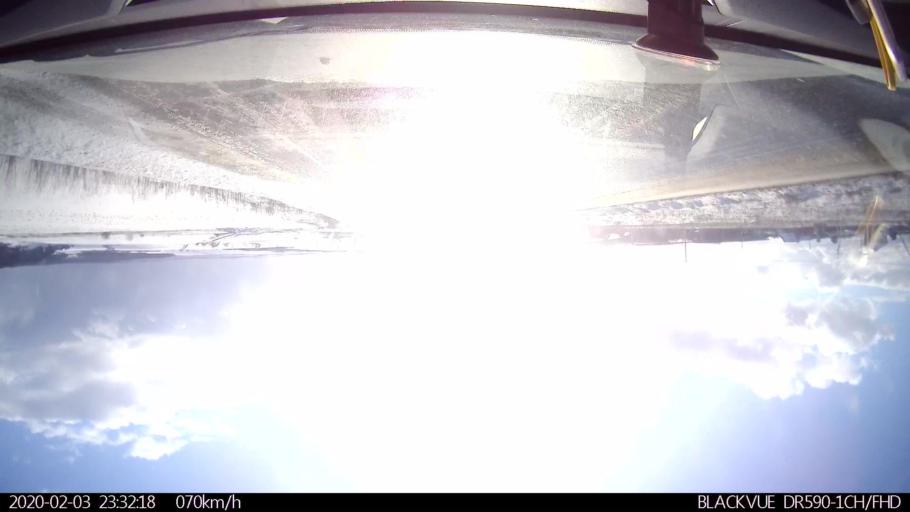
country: RU
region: Nizjnij Novgorod
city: Dal'neye Konstantinovo
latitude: 55.9333
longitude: 44.2289
